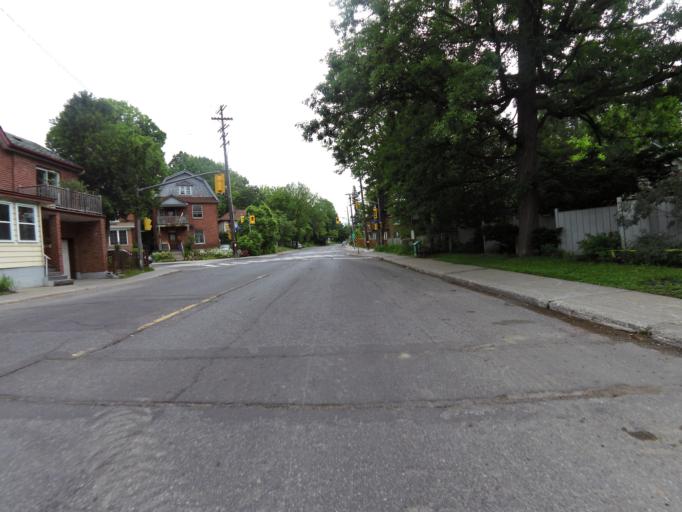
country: CA
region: Ontario
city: Ottawa
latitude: 45.3956
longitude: -75.6790
